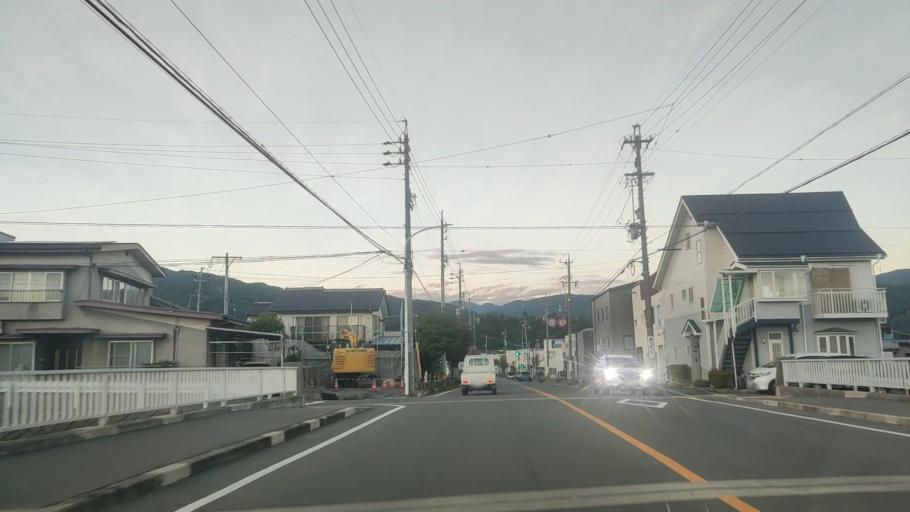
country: JP
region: Nagano
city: Okaya
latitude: 36.0730
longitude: 138.0614
